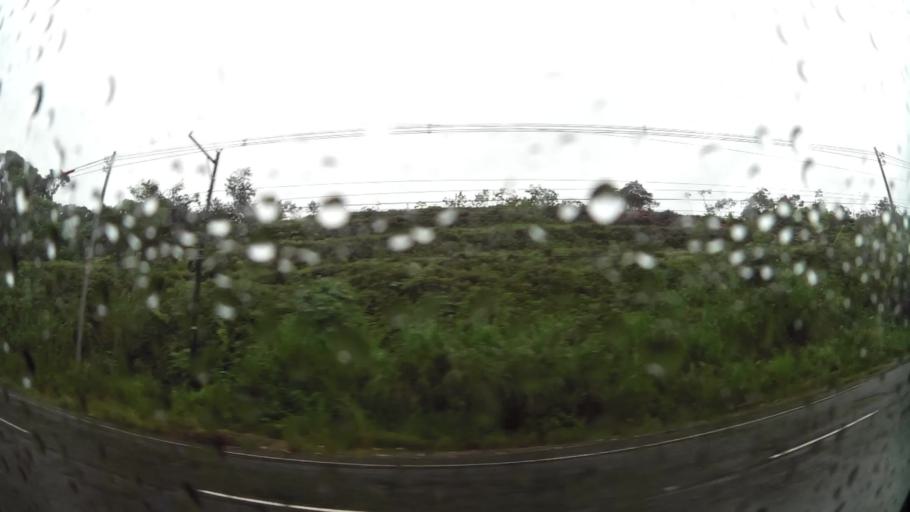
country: PA
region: Colon
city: Gatun
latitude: 9.2890
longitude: -79.7534
